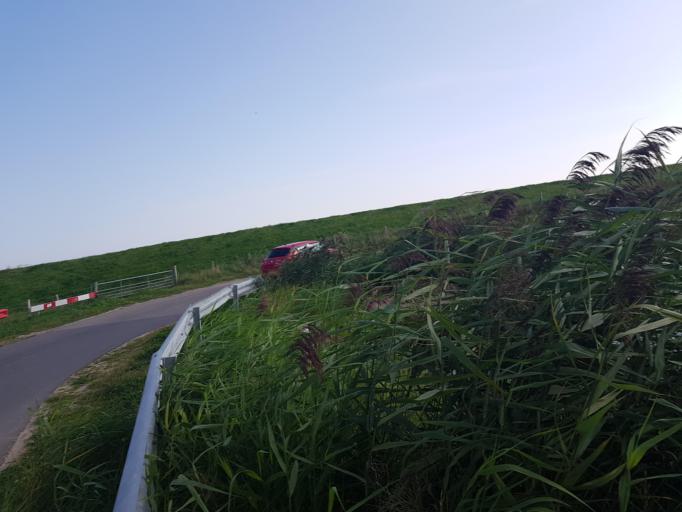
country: NL
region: North Holland
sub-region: Gemeente Texel
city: Den Burg
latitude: 53.1096
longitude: 4.8670
